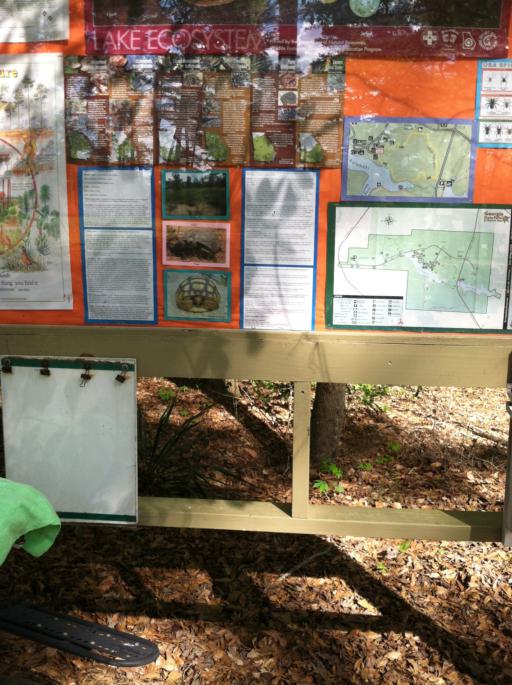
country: US
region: Georgia
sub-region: Early County
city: Blakely
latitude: 31.4667
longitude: -84.9276
